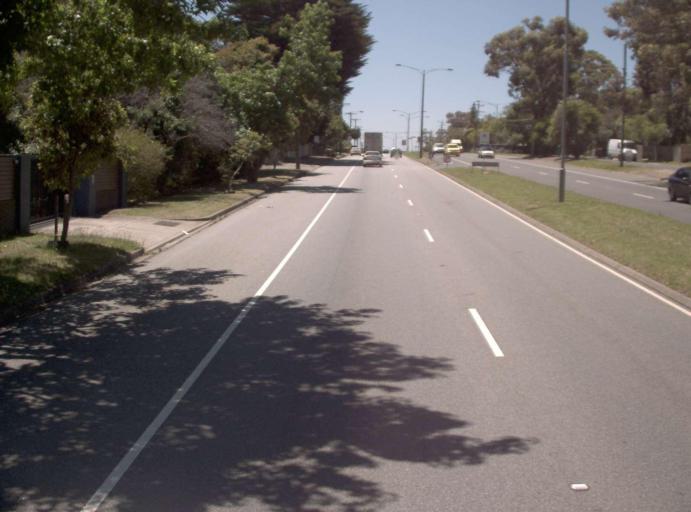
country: AU
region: Victoria
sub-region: Frankston
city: Frankston
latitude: -38.1623
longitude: 145.1028
